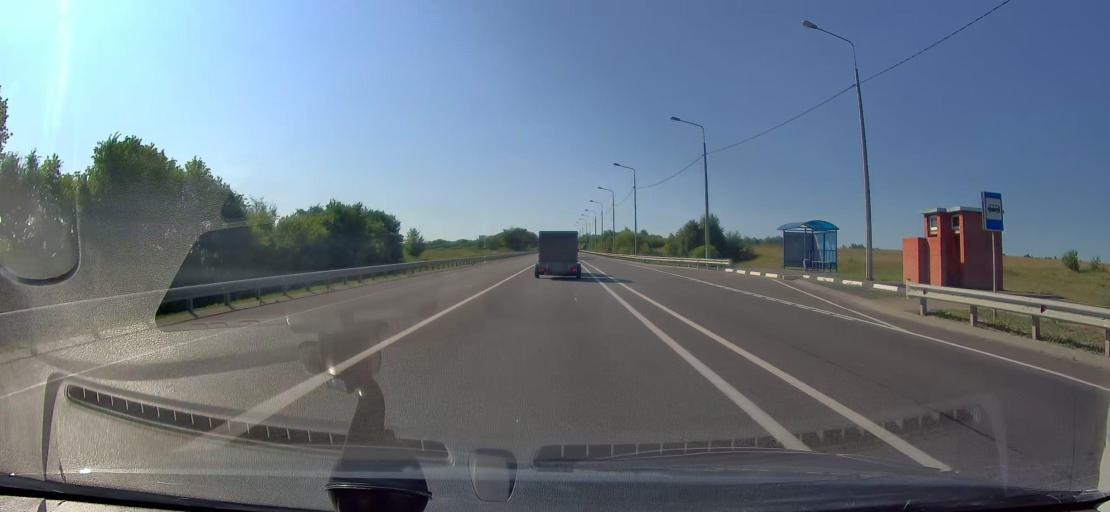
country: RU
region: Orjol
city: Kromy
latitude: 52.6390
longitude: 35.7492
